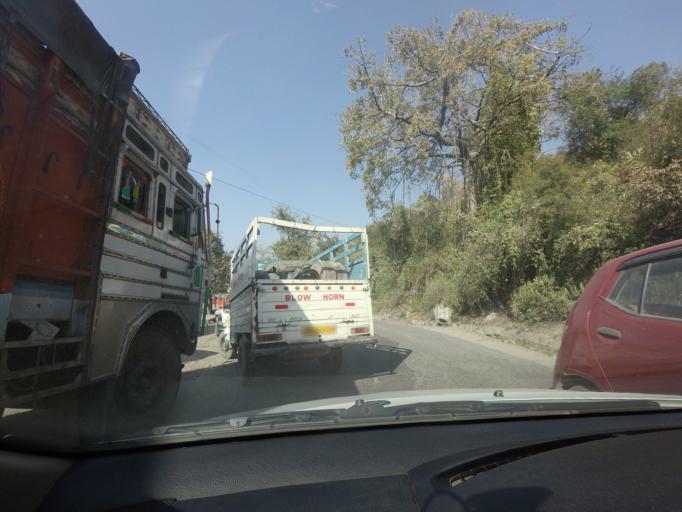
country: IN
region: Himachal Pradesh
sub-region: Solan
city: Arki
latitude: 31.2581
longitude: 76.9144
